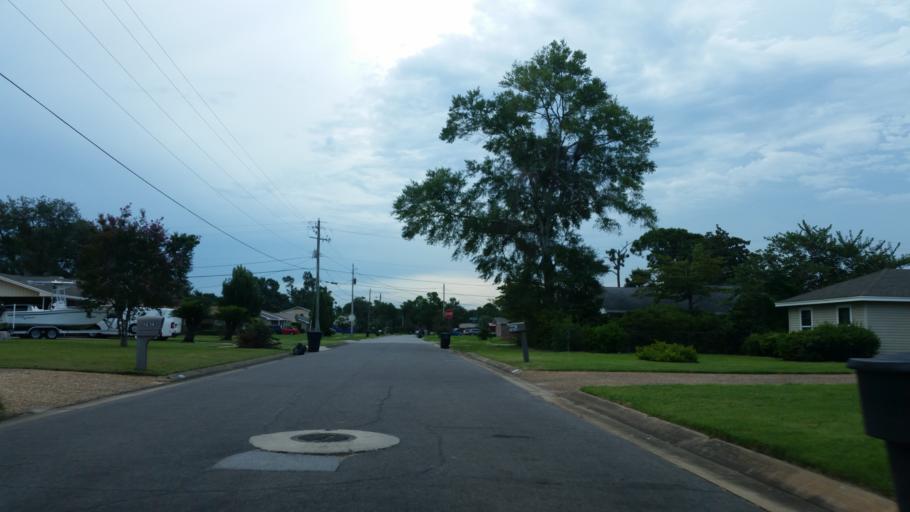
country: US
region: Florida
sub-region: Escambia County
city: Ferry Pass
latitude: 30.5038
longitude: -87.1830
